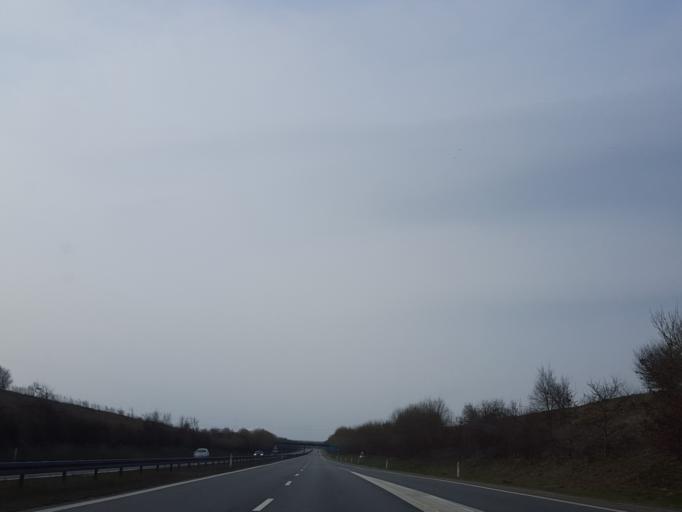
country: DK
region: South Denmark
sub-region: Esbjerg Kommune
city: Esbjerg
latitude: 55.5060
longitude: 8.5026
